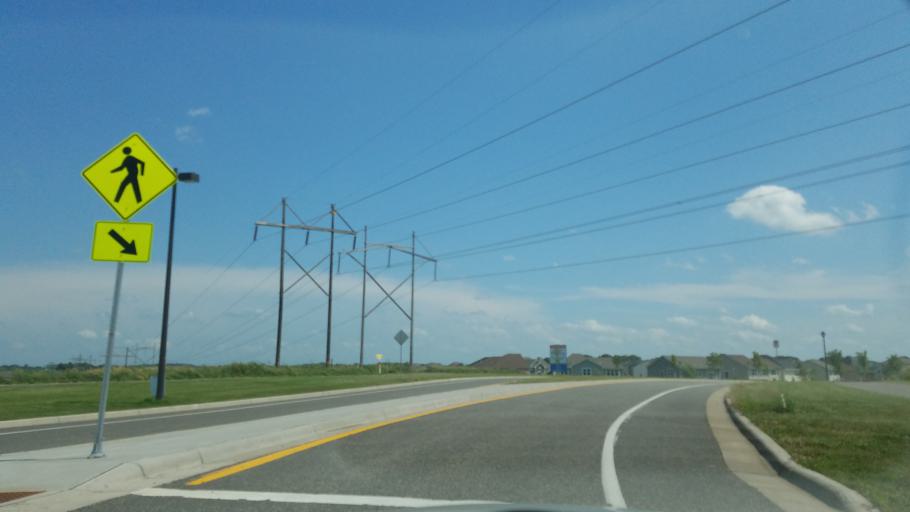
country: US
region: Minnesota
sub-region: Washington County
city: Woodbury
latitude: 44.8839
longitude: -92.9247
